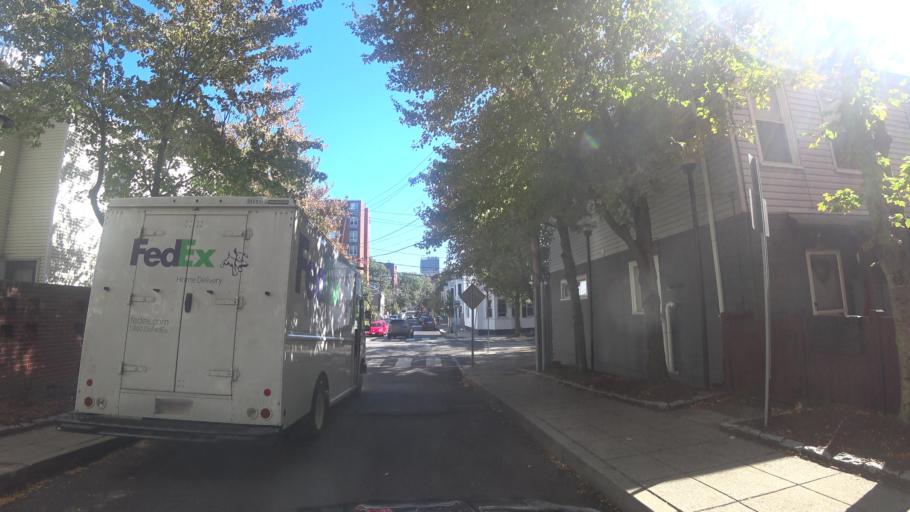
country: US
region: Massachusetts
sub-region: Middlesex County
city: Cambridge
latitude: 42.3710
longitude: -71.0881
